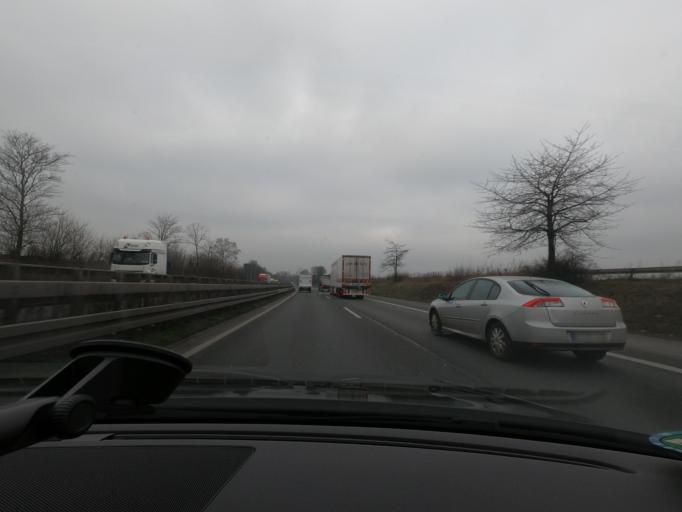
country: DE
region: North Rhine-Westphalia
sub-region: Regierungsbezirk Dusseldorf
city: Monchengladbach
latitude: 51.1226
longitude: 6.4275
